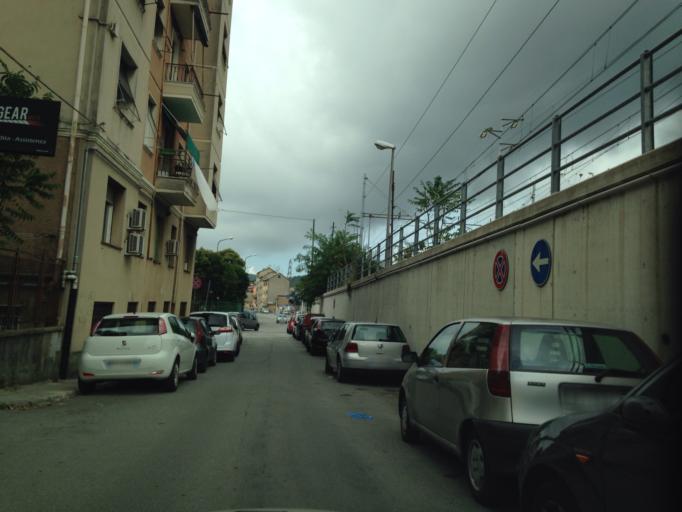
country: IT
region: Liguria
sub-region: Provincia di Genova
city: Genoa
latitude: 44.4553
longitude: 8.8974
